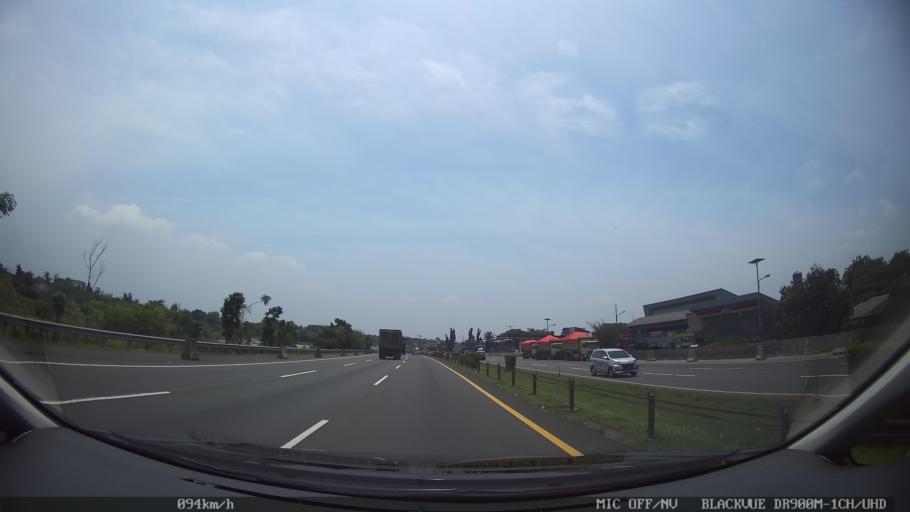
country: ID
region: West Java
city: Kresek
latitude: -6.1877
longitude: 106.4091
